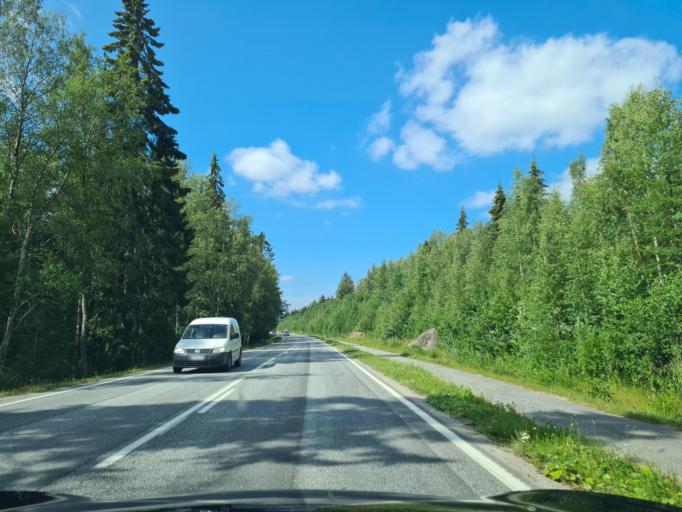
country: FI
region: Ostrobothnia
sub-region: Vaasa
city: Vaasa
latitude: 63.1966
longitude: 21.5441
